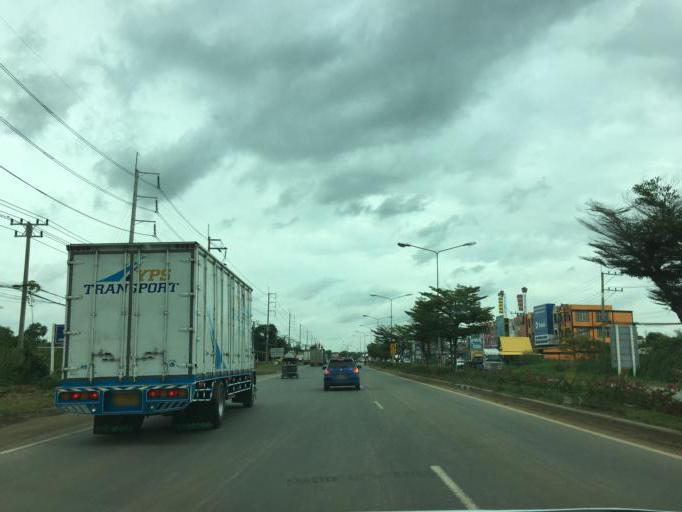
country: TH
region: Phra Nakhon Si Ayutthaya
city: Wang Noi
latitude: 14.2716
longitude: 100.6849
